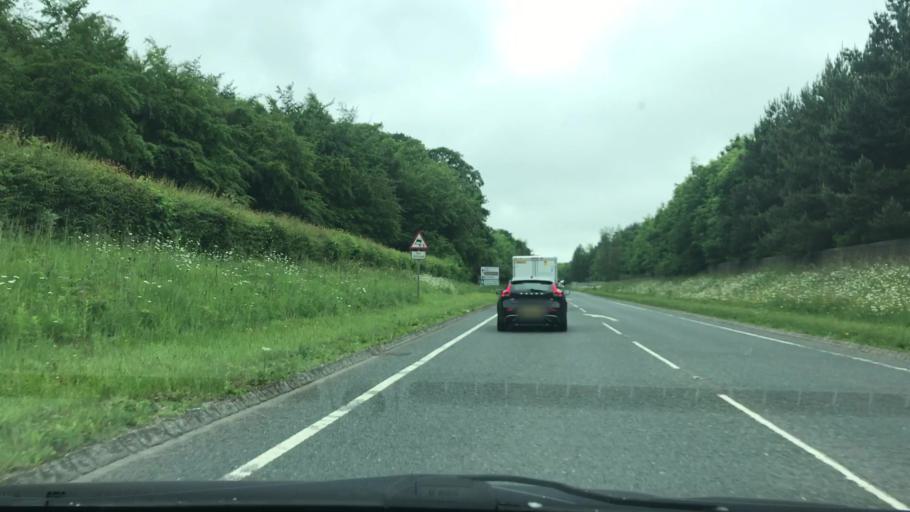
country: GB
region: England
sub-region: North Yorkshire
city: Knaresborough
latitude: 53.9686
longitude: -1.4885
